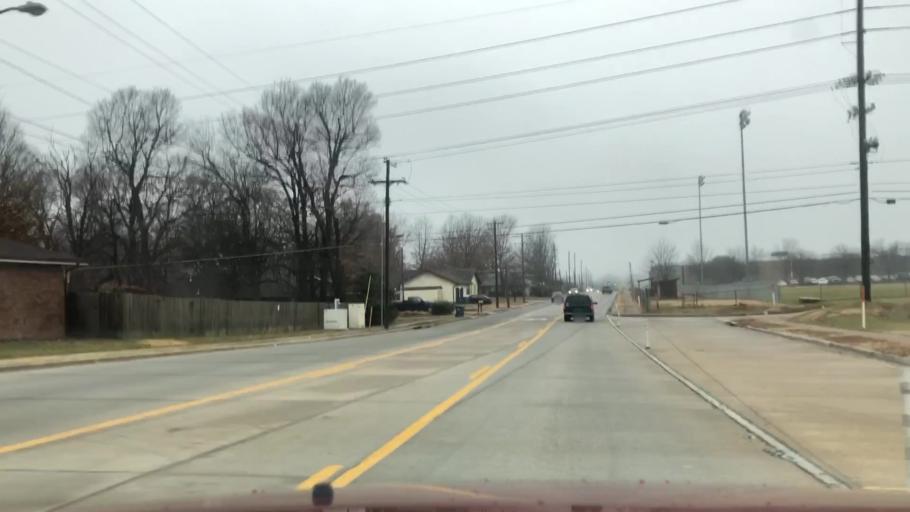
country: US
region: Missouri
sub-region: Greene County
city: Springfield
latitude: 37.1455
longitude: -93.2865
